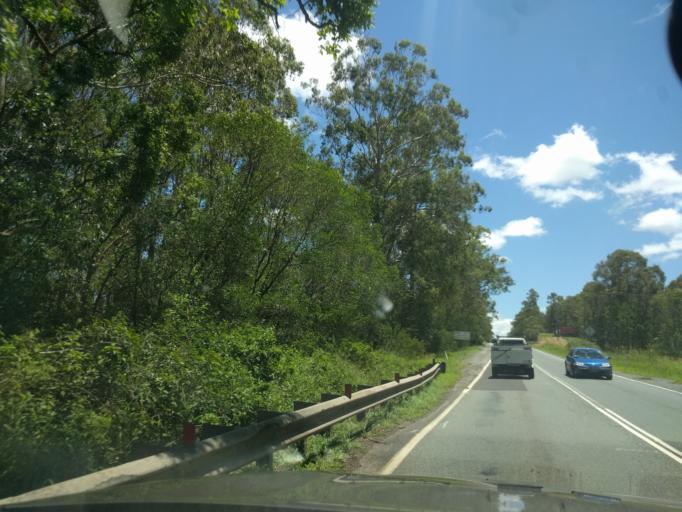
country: AU
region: Queensland
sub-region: Logan
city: Cedar Vale
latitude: -27.8431
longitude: 153.0226
